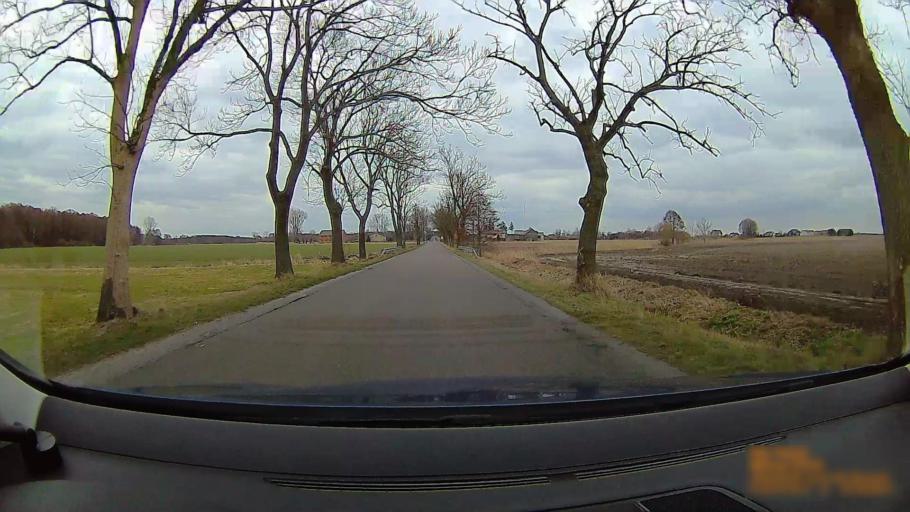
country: PL
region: Greater Poland Voivodeship
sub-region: Powiat koninski
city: Rzgow Pierwszy
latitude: 52.1265
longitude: 18.0582
